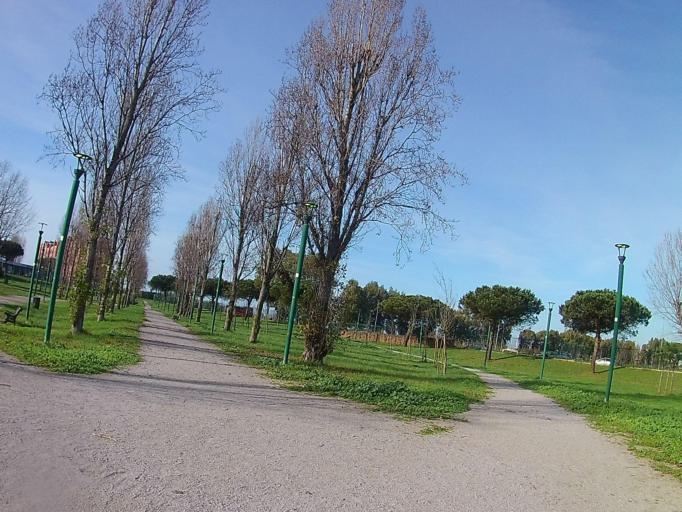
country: IT
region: Latium
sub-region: Citta metropolitana di Roma Capitale
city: Lido di Ostia
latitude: 41.7421
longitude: 12.2627
